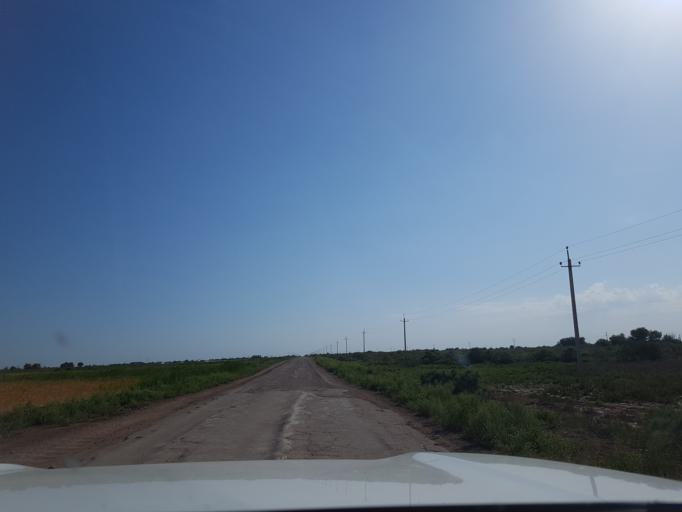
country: TM
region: Dasoguz
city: Koeneuergench
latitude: 42.0577
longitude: 58.8409
